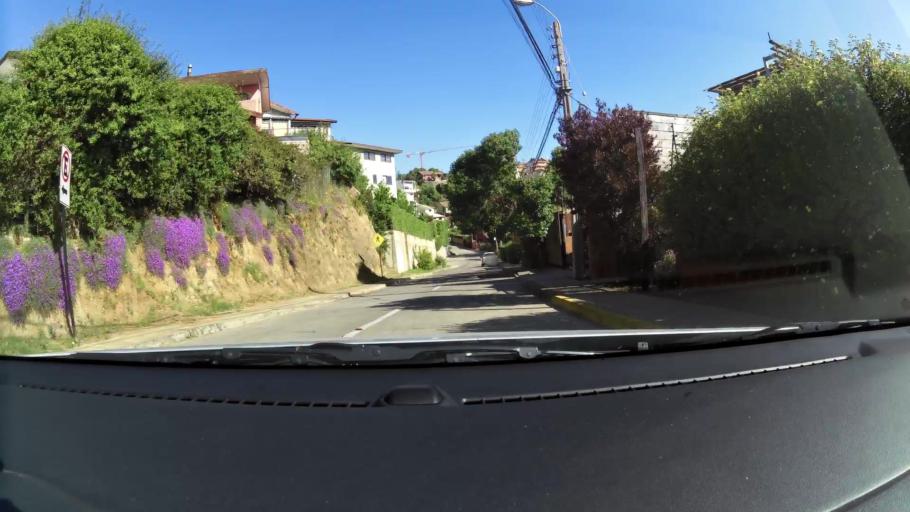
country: CL
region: Valparaiso
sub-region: Provincia de Valparaiso
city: Vina del Mar
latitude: -33.0365
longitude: -71.5583
